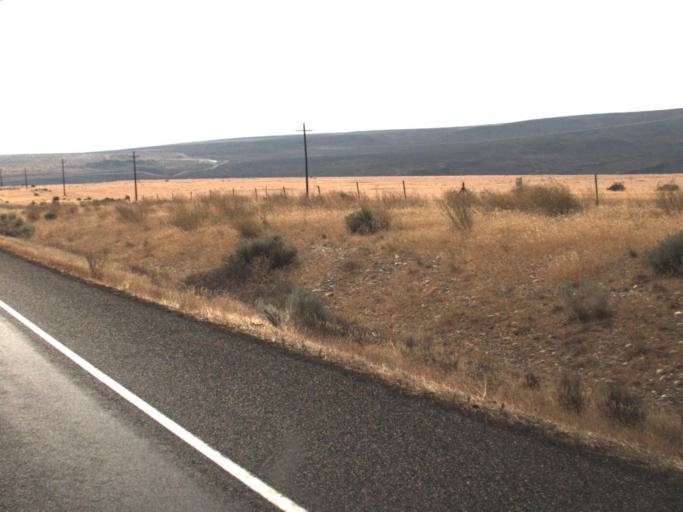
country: US
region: Washington
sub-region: Grant County
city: Desert Aire
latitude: 46.6300
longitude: -119.7267
